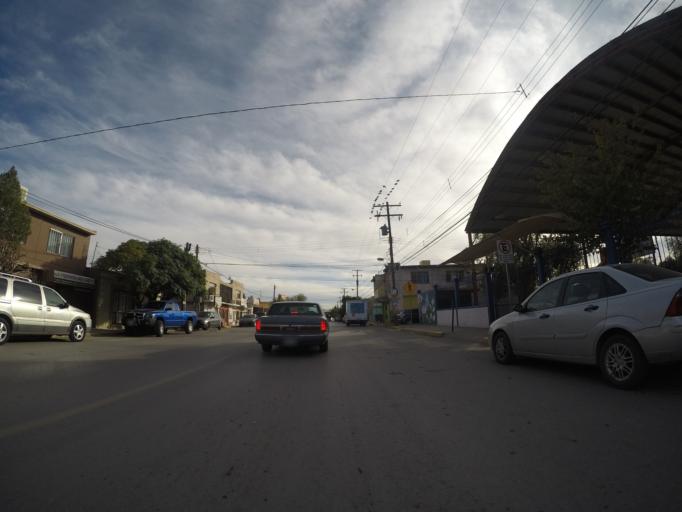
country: MX
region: Chihuahua
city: Ciudad Juarez
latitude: 31.7279
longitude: -106.4279
